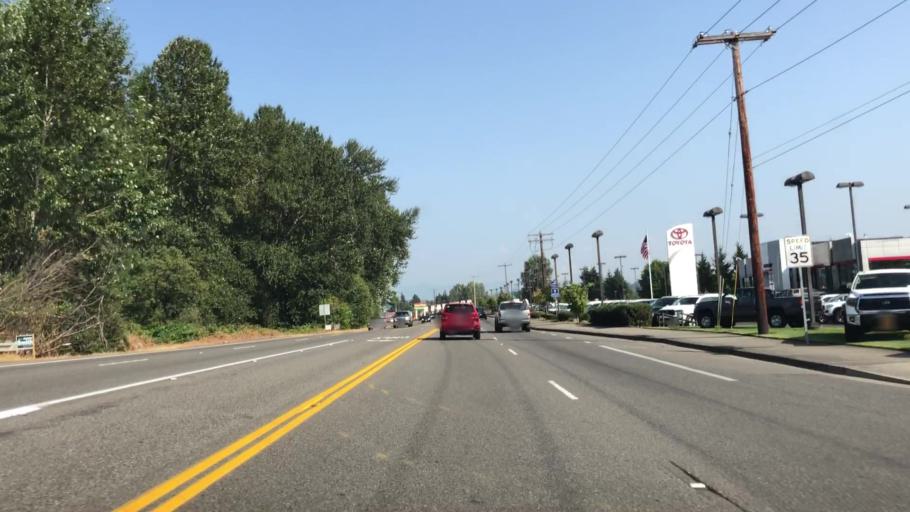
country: US
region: Washington
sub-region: Pierce County
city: Puyallup
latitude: 47.2044
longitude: -122.3136
